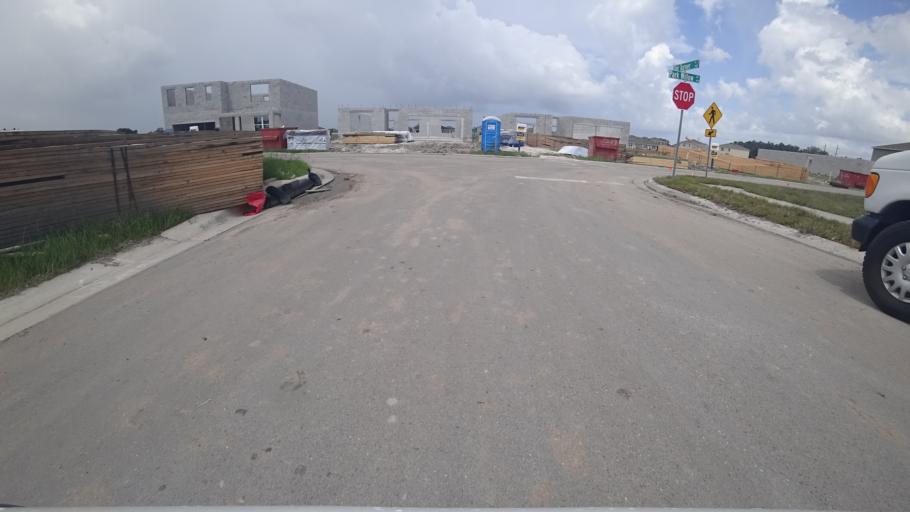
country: US
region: Florida
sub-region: Manatee County
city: Ellenton
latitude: 27.5490
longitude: -82.5131
